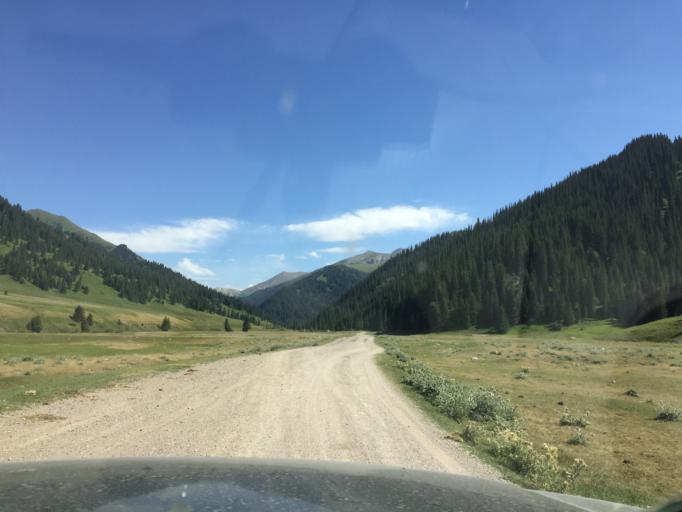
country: KZ
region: Almaty Oblysy
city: Kegen
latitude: 42.6734
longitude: 79.2003
